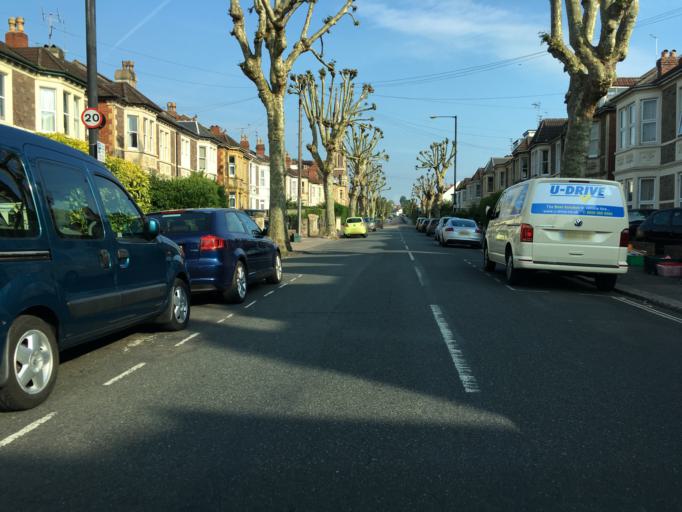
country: GB
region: England
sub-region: Bristol
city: Bristol
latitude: 51.4723
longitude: -2.5968
